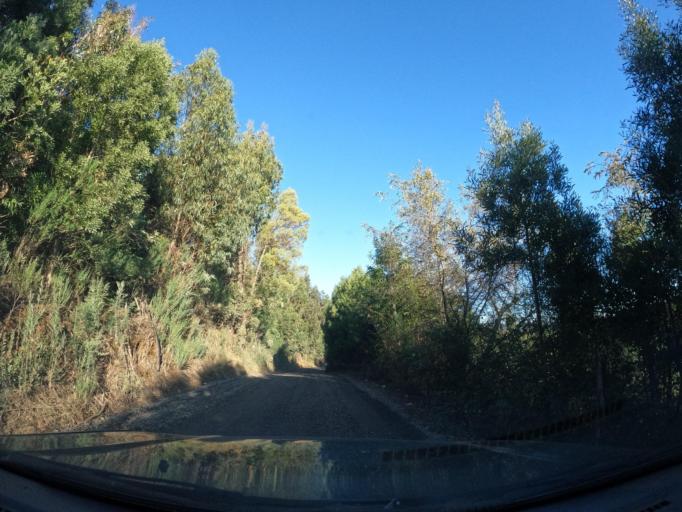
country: CL
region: Biobio
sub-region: Provincia de Concepcion
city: Chiguayante
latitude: -37.0285
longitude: -72.8721
